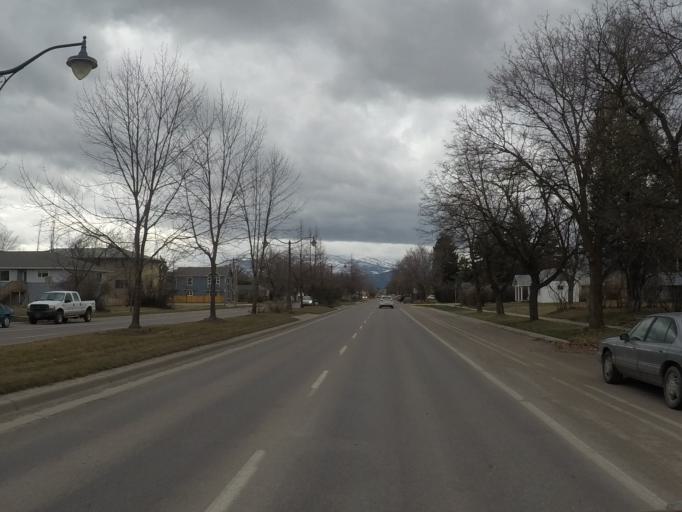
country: US
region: Montana
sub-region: Missoula County
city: Missoula
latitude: 46.8597
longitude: -114.0086
